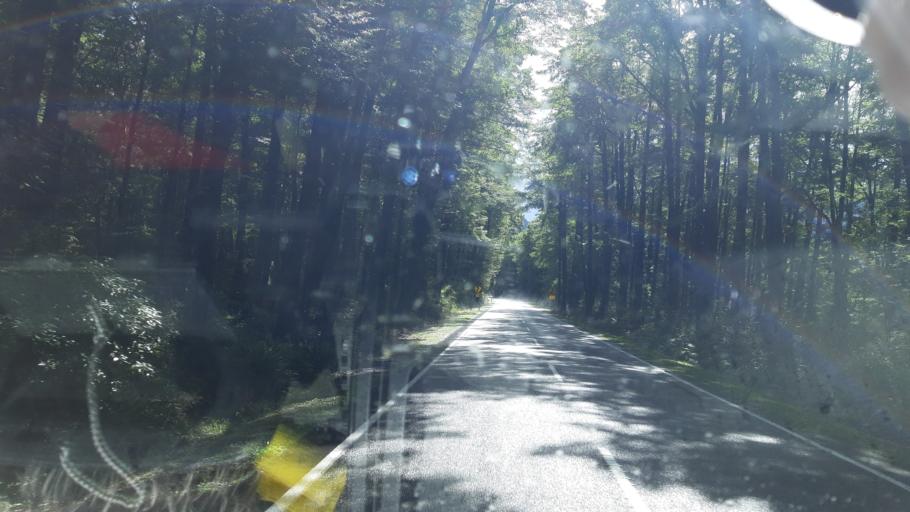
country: NZ
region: West Coast
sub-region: Buller District
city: Westport
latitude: -42.3756
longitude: 172.2725
